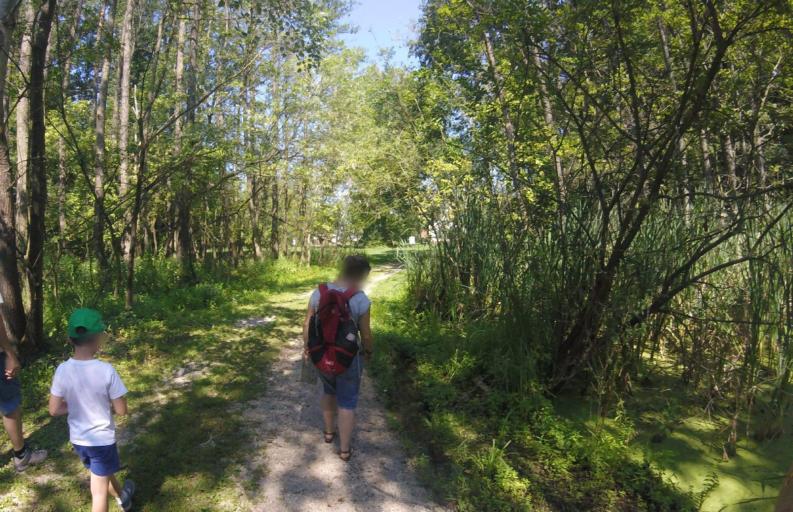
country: HU
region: Zala
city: Sarmellek
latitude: 46.6779
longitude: 17.2305
